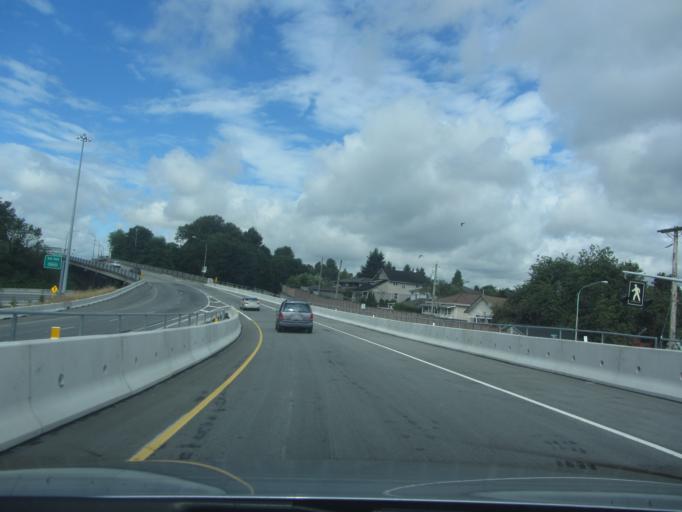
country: CA
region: British Columbia
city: Burnaby
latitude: 49.2583
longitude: -123.0174
